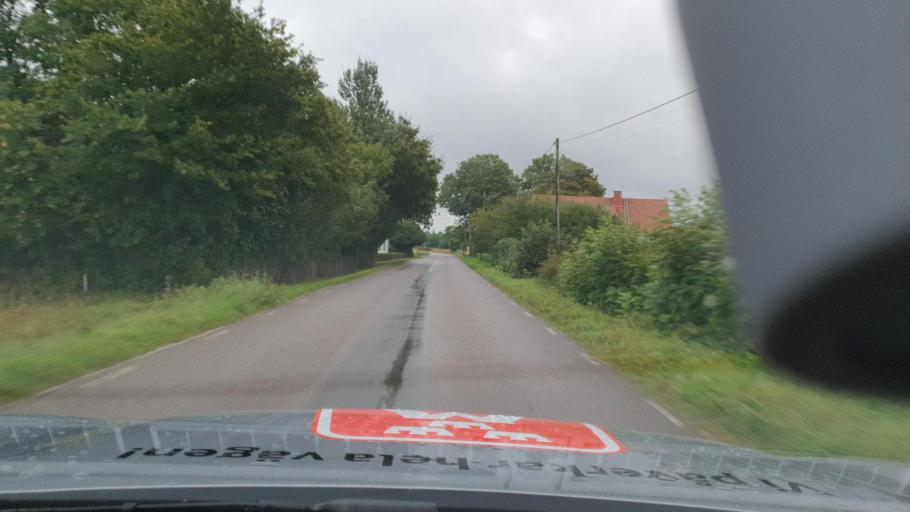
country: SE
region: Gotland
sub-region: Gotland
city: Visby
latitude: 57.7803
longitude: 18.5050
